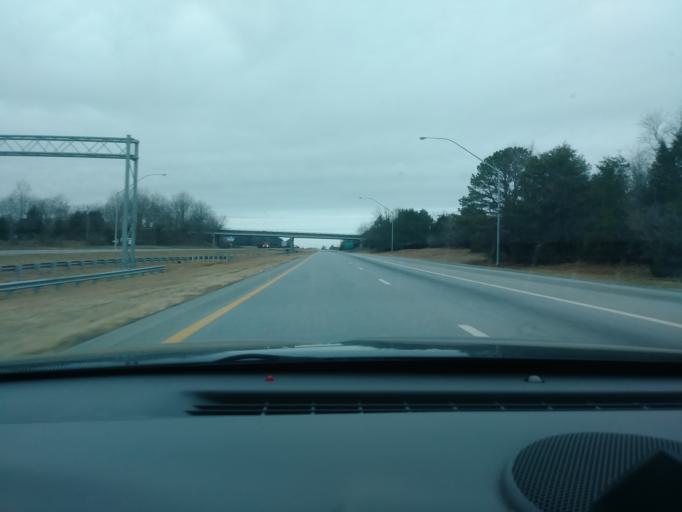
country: US
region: North Carolina
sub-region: Yadkin County
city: Jonesville
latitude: 36.1233
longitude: -80.8184
